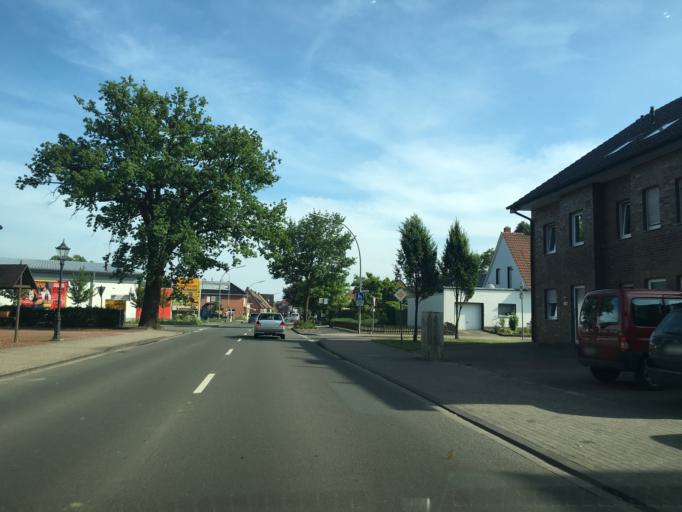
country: DE
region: North Rhine-Westphalia
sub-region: Regierungsbezirk Munster
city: Nordwalde
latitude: 52.0933
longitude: 7.4789
